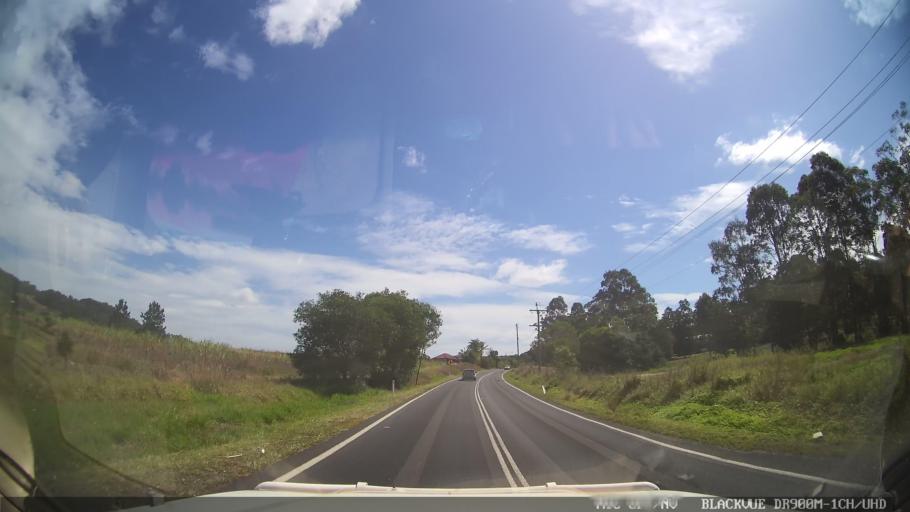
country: AU
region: Queensland
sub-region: Sunshine Coast
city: Twin Waters
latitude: -26.6140
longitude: 153.0106
